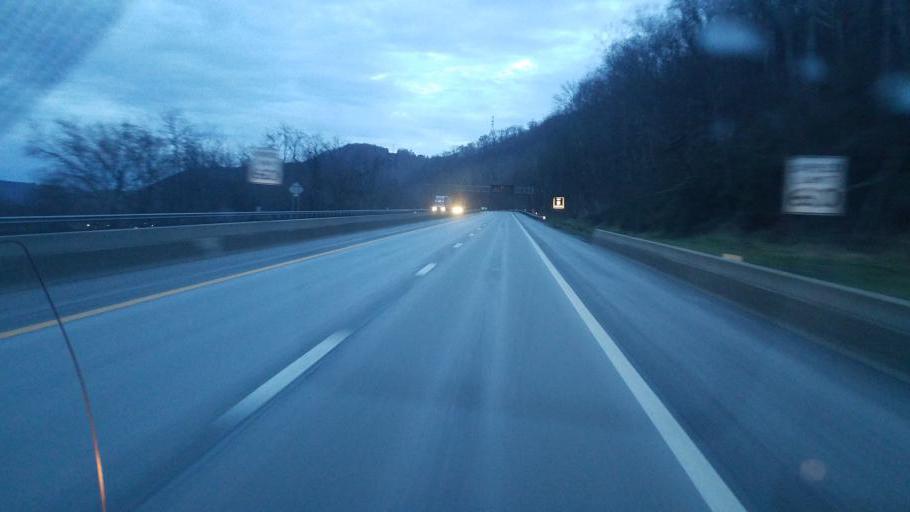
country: US
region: West Virginia
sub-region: Kanawha County
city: Chesapeake
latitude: 38.1924
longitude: -81.4951
